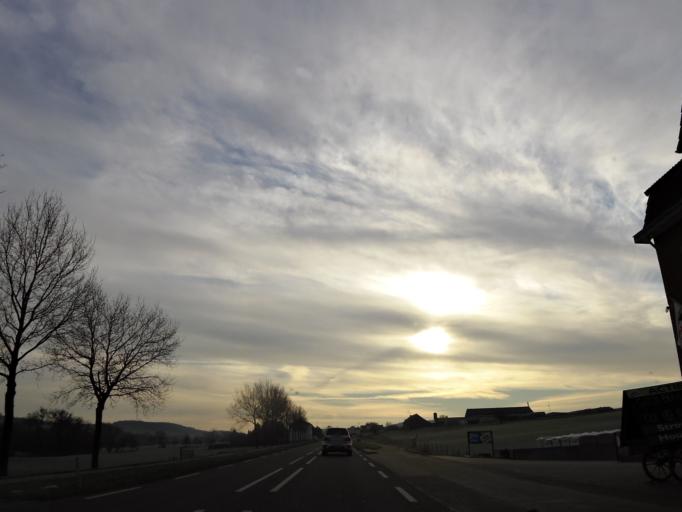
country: NL
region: Limburg
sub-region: Gemeente Simpelveld
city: Simpelveld
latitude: 50.7960
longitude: 5.9752
